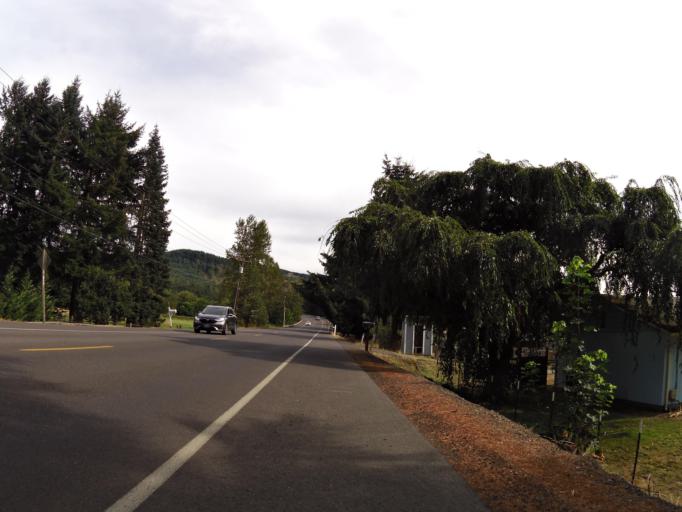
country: US
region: Washington
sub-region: Cowlitz County
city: Castle Rock
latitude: 46.2620
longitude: -122.8946
